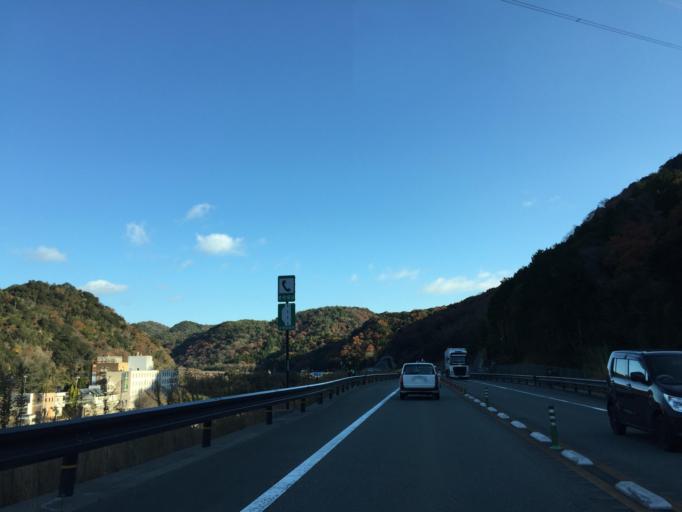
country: JP
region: Wakayama
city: Wakayama-shi
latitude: 34.3017
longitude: 135.1578
